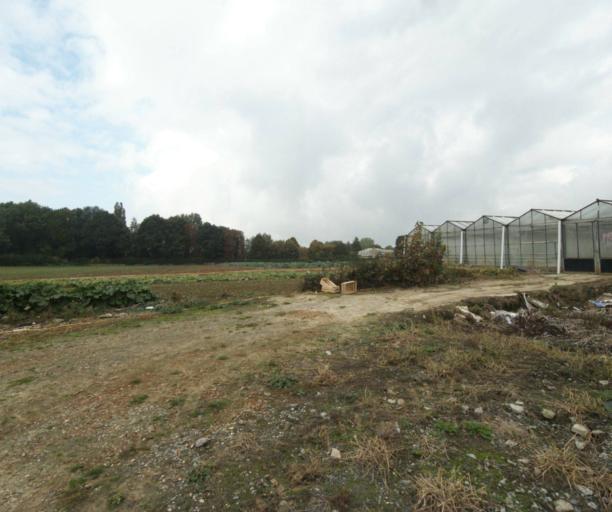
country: FR
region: Nord-Pas-de-Calais
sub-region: Departement du Nord
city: Fournes-en-Weppes
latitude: 50.5818
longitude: 2.8872
